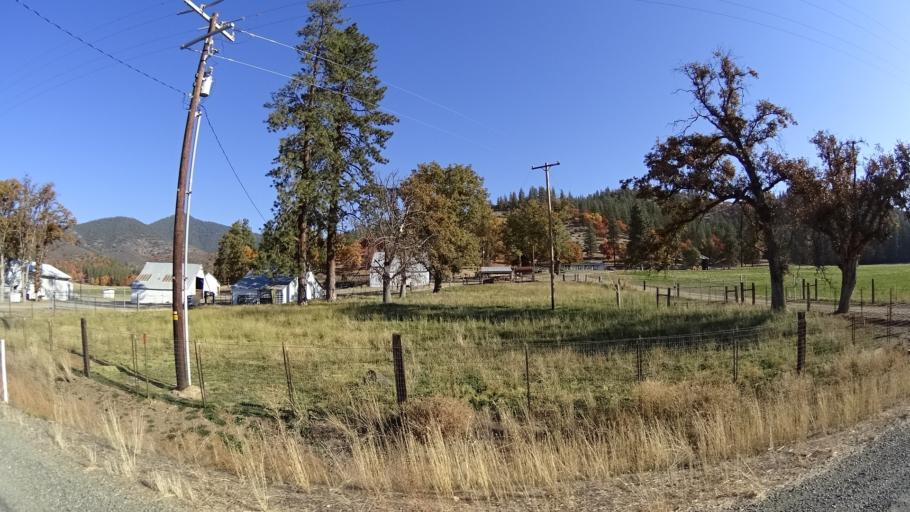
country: US
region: California
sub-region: Siskiyou County
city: Yreka
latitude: 41.6386
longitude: -122.9105
